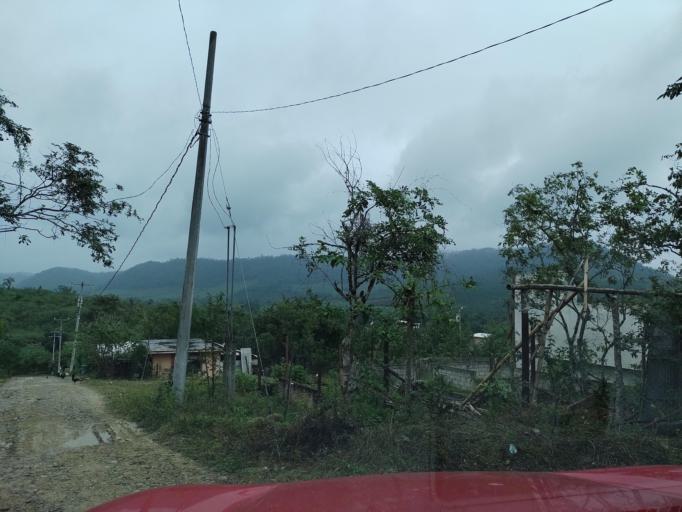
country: MX
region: Veracruz
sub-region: Papantla
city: El Chote
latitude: 20.3964
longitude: -97.3166
